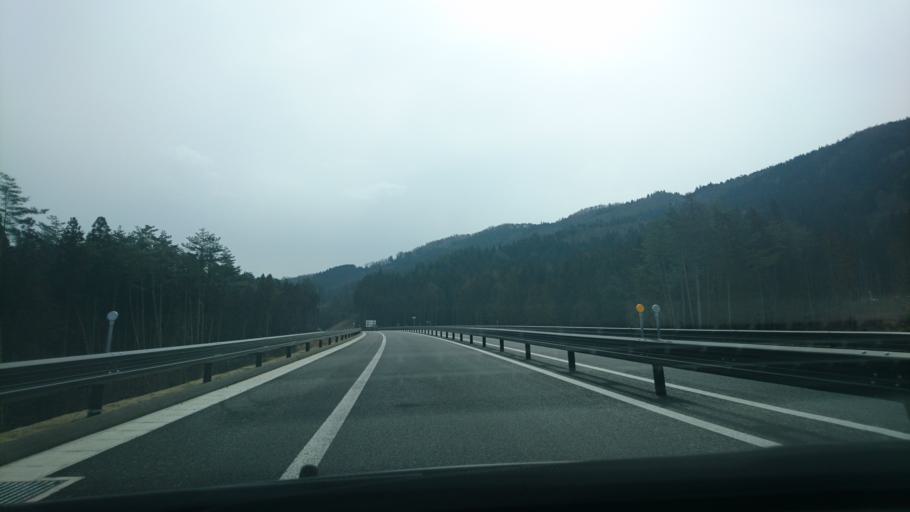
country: JP
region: Iwate
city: Tono
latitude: 39.2704
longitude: 141.5723
